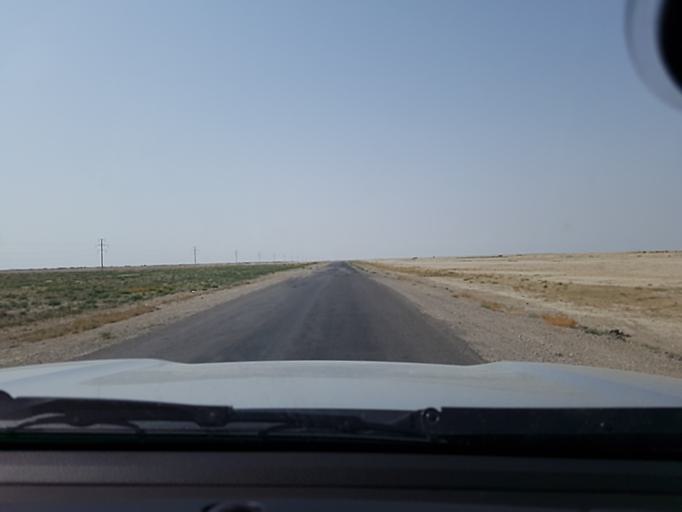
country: TM
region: Balkan
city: Gumdag
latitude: 38.8541
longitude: 54.5952
